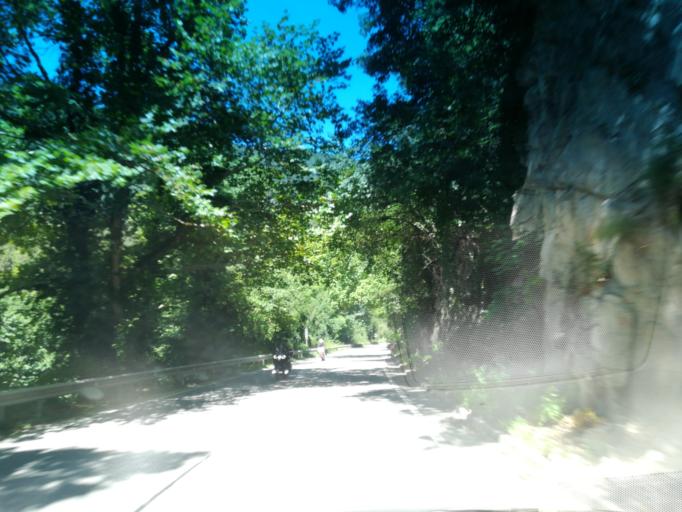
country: BG
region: Plovdiv
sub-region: Obshtina Asenovgrad
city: Asenovgrad
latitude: 41.9416
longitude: 24.8482
